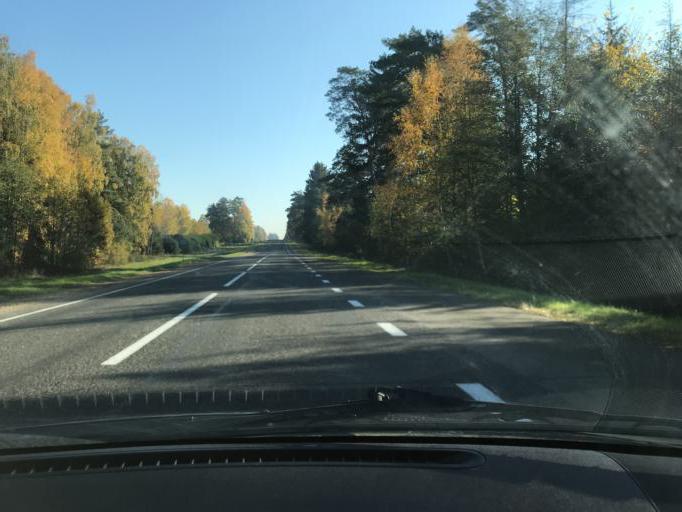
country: BY
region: Brest
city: Lyakhavichy
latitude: 52.9550
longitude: 26.2726
